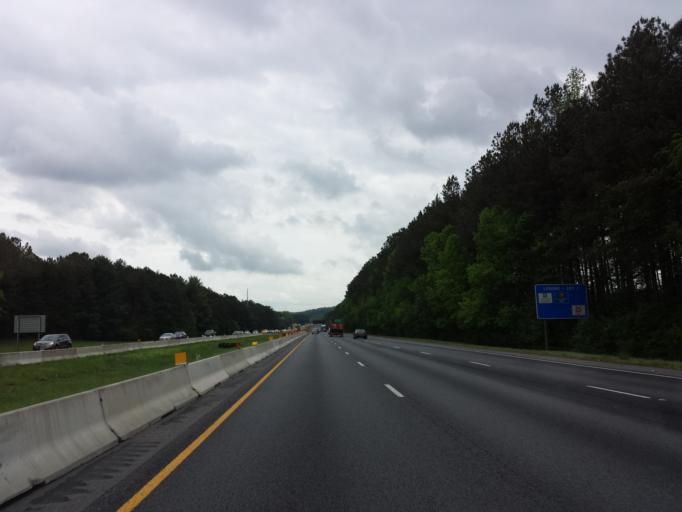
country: US
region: Georgia
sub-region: Cobb County
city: Kennesaw
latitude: 34.0330
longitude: -84.5616
